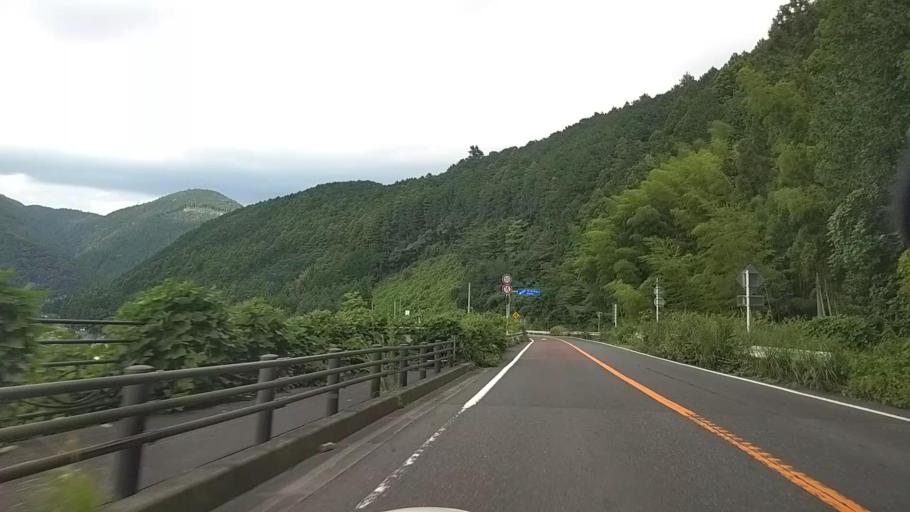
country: JP
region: Shizuoka
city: Fujinomiya
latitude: 35.2169
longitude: 138.5187
